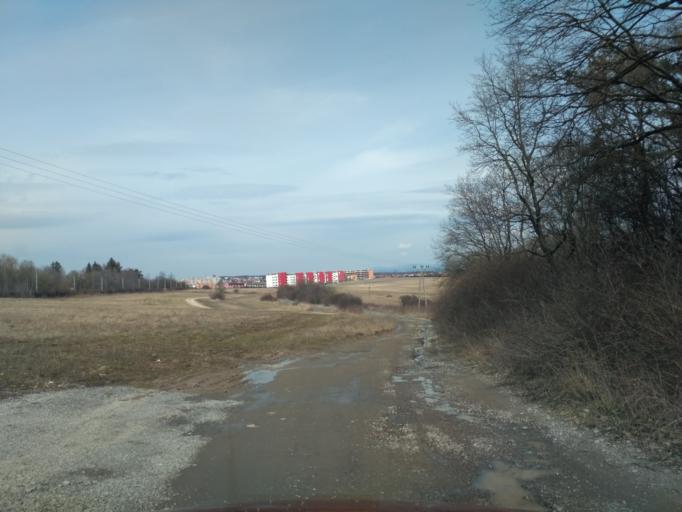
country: SK
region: Kosicky
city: Kosice
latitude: 48.7131
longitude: 21.2933
